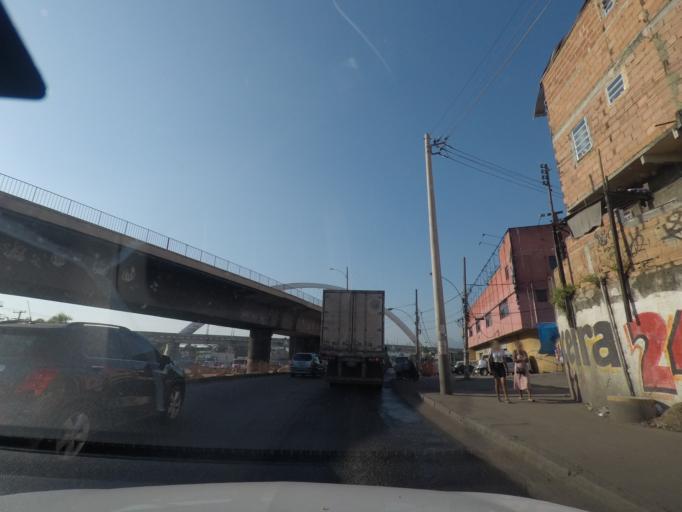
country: BR
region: Rio de Janeiro
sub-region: Rio De Janeiro
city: Rio de Janeiro
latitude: -22.8483
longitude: -43.2475
